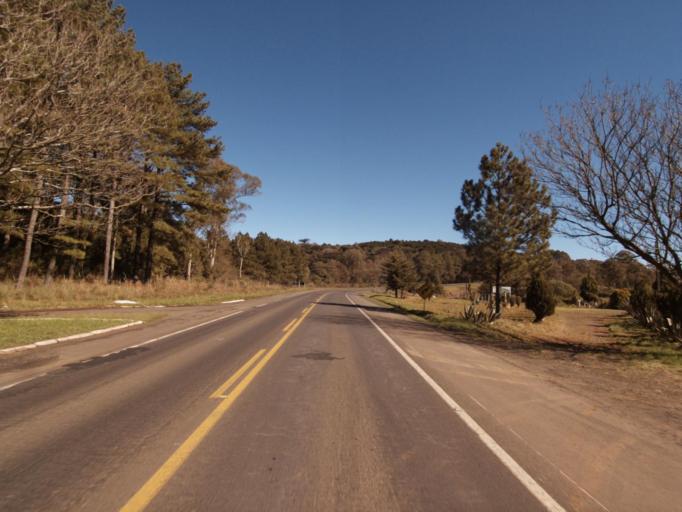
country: BR
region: Santa Catarina
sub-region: Joacaba
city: Joacaba
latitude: -27.1599
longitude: -51.5817
